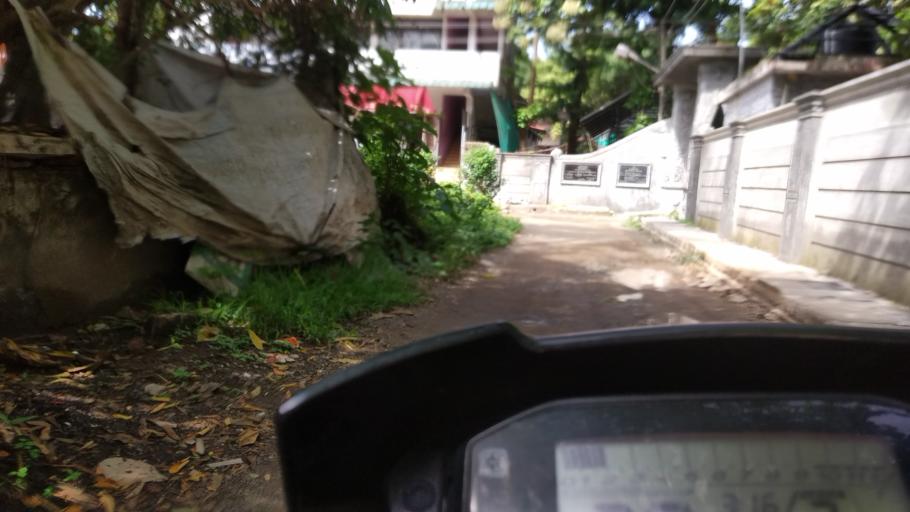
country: IN
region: Kerala
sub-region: Ernakulam
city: Cochin
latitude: 9.9827
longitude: 76.2916
